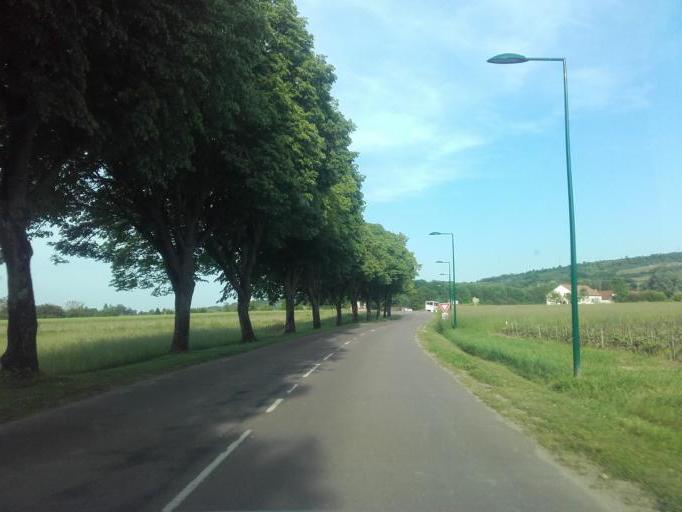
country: FR
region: Bourgogne
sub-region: Departement de Saone-et-Loire
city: Chagny
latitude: 46.9080
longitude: 4.7087
